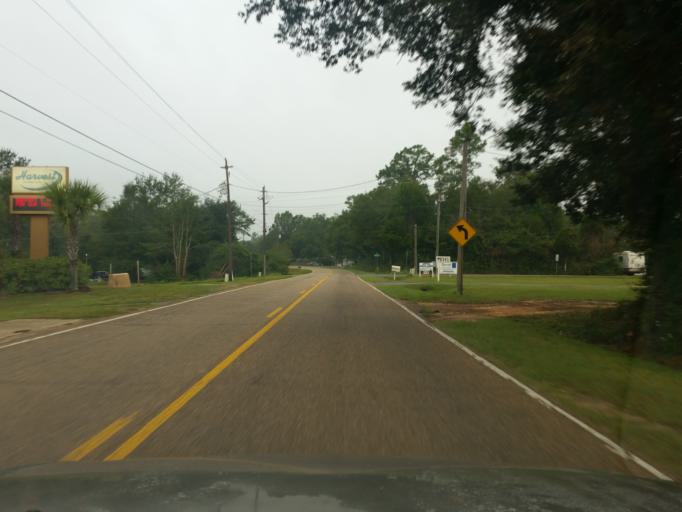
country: US
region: Florida
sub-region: Escambia County
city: Cantonment
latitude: 30.6072
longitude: -87.3522
